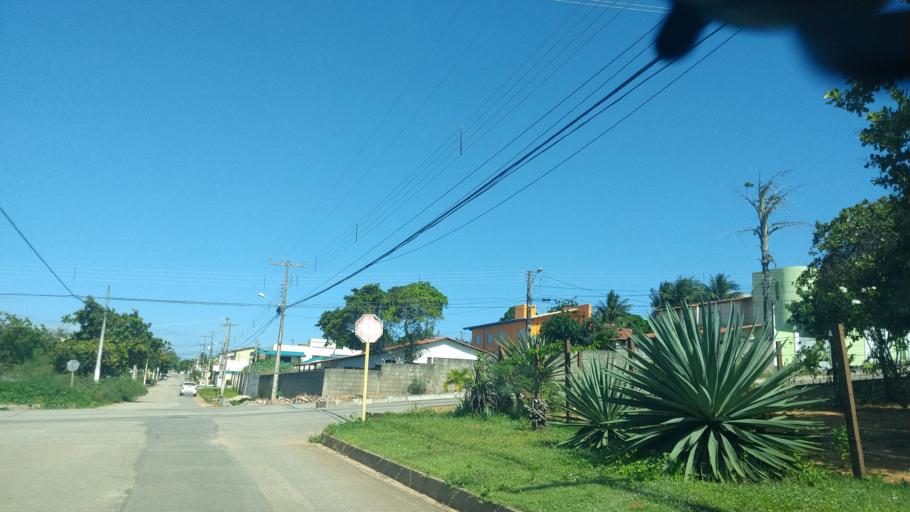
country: BR
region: Rio Grande do Norte
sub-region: Natal
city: Natal
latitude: -5.8464
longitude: -35.2036
